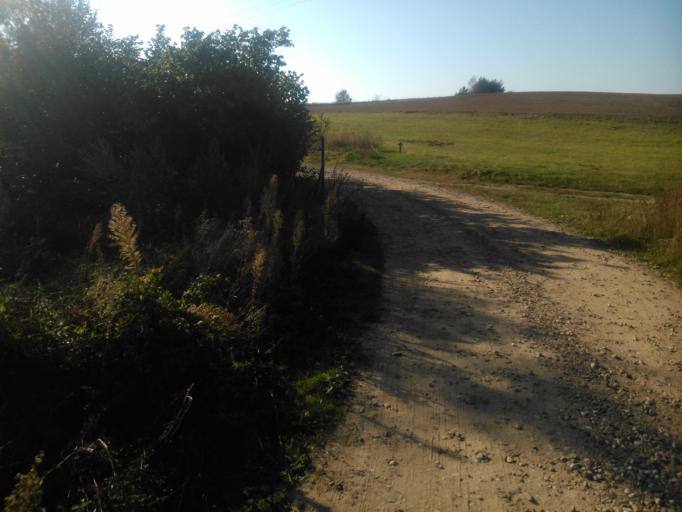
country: PL
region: Kujawsko-Pomorskie
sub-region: Powiat brodnicki
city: Gorzno
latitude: 53.2091
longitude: 19.6612
